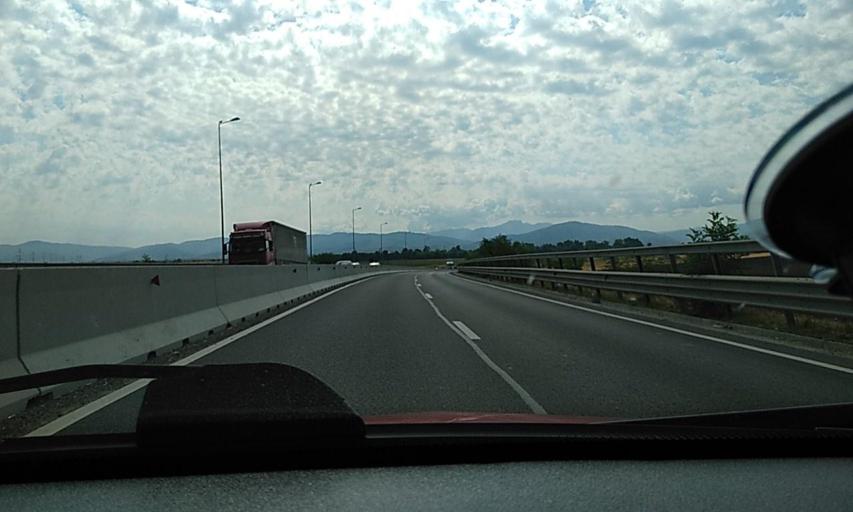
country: RO
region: Brasov
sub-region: Comuna Sanpetru
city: Sanpetru
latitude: 45.6801
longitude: 25.6632
